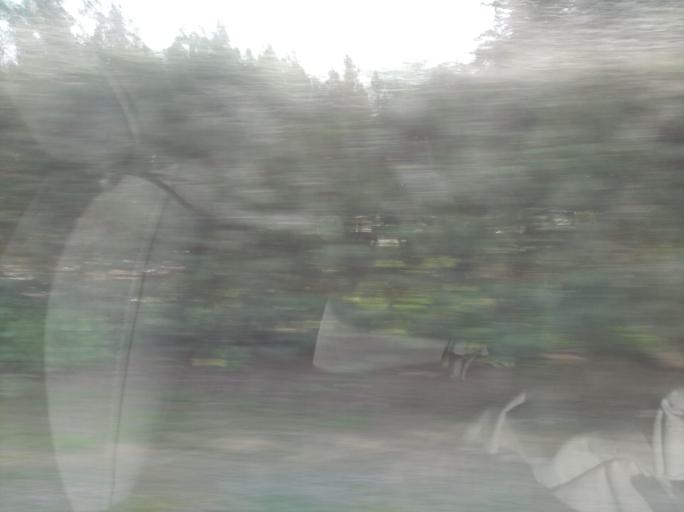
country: CL
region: Valparaiso
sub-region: Provincia de Marga Marga
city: Limache
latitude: -33.0115
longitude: -71.2138
